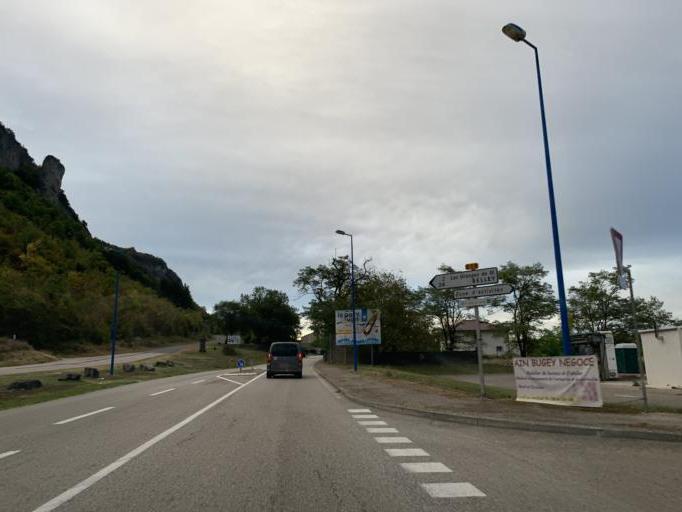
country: FR
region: Rhone-Alpes
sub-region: Departement de l'Isere
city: Bouvesse-Quirieu
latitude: 45.8121
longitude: 5.4523
